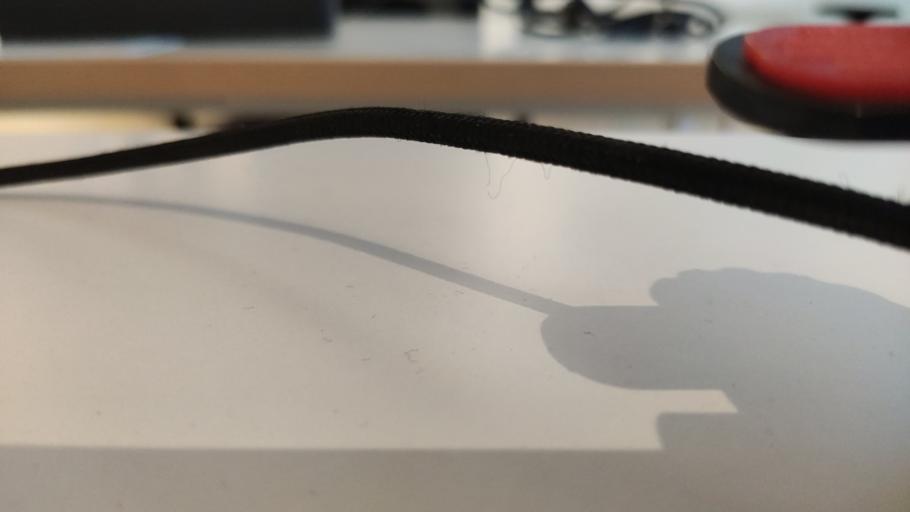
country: RU
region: Moskovskaya
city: Novopetrovskoye
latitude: 55.8661
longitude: 36.3921
